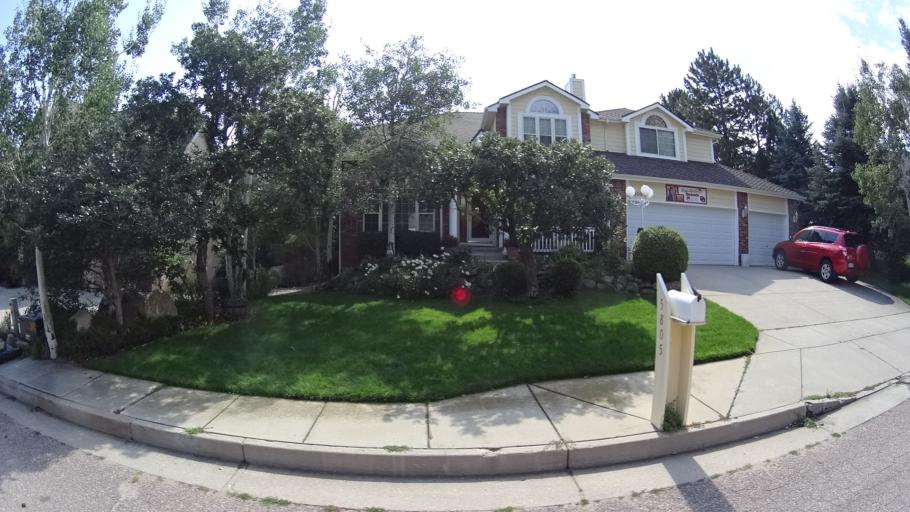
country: US
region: Colorado
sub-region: El Paso County
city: Fort Carson
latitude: 38.7469
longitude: -104.8316
